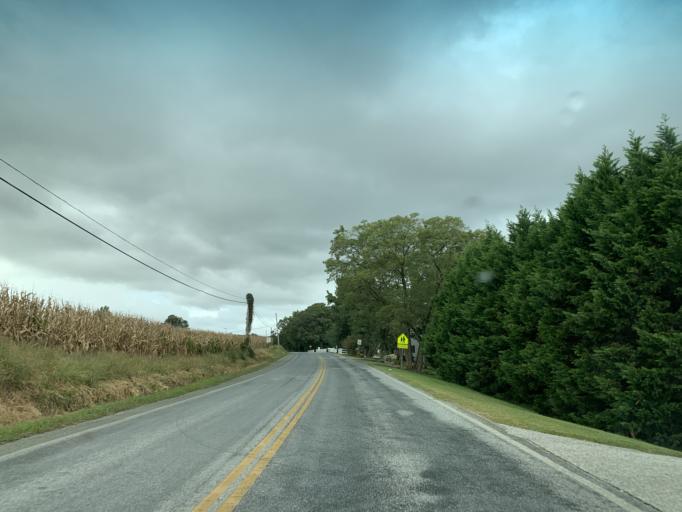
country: US
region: Maryland
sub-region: Caroline County
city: Denton
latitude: 38.9064
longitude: -75.8390
